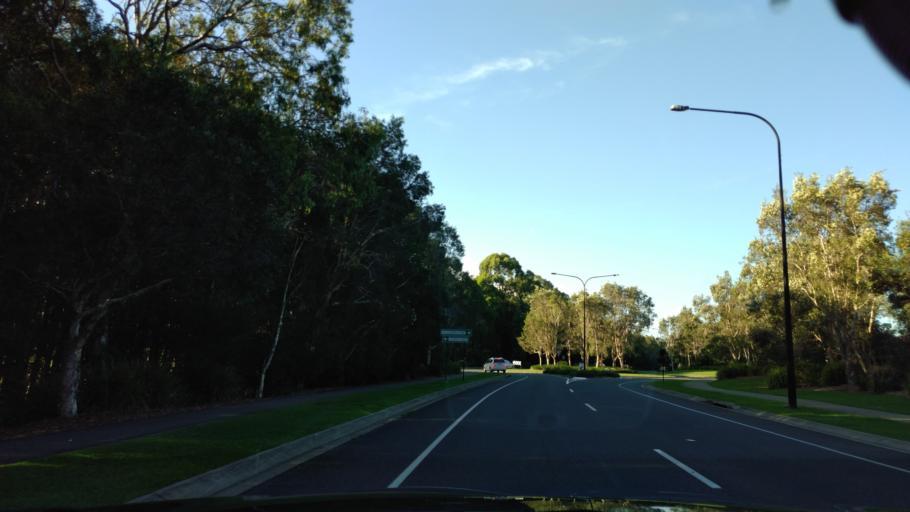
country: AU
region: Queensland
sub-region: Moreton Bay
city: Mango Hill
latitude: -27.2260
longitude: 153.0213
